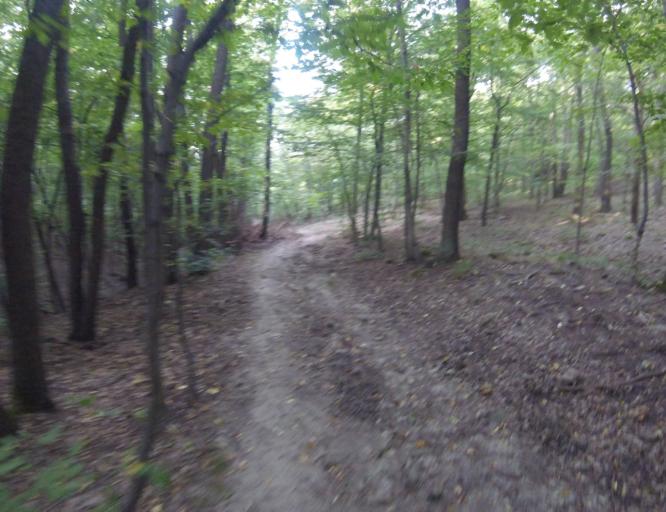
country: HU
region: Pest
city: Nagykovacsi
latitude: 47.6795
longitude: 19.0125
